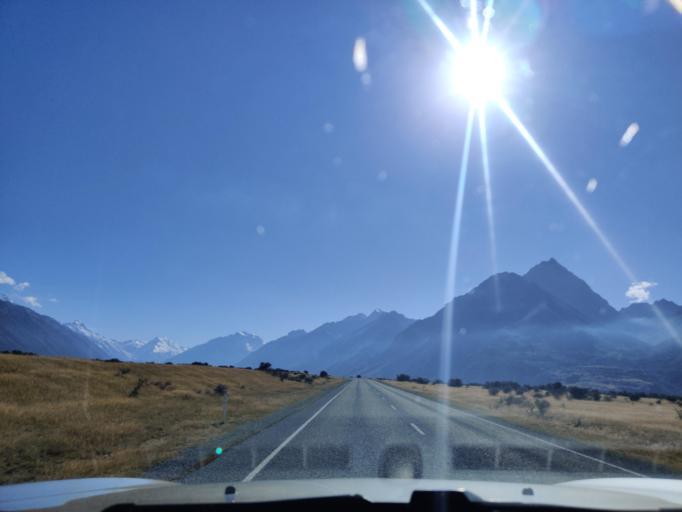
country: NZ
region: Canterbury
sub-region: Timaru District
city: Pleasant Point
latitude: -43.7851
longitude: 170.1211
